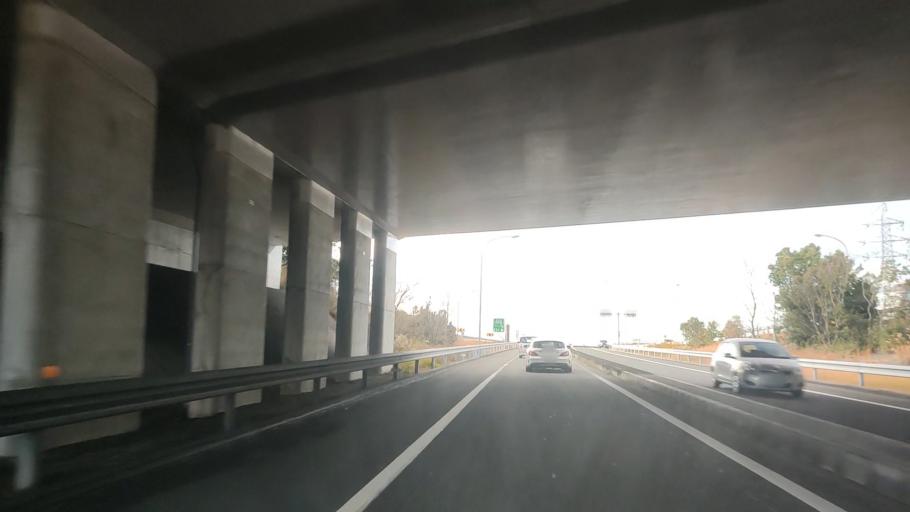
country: JP
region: Ehime
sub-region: Shikoku-chuo Shi
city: Matsuyama
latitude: 33.7949
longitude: 132.7807
